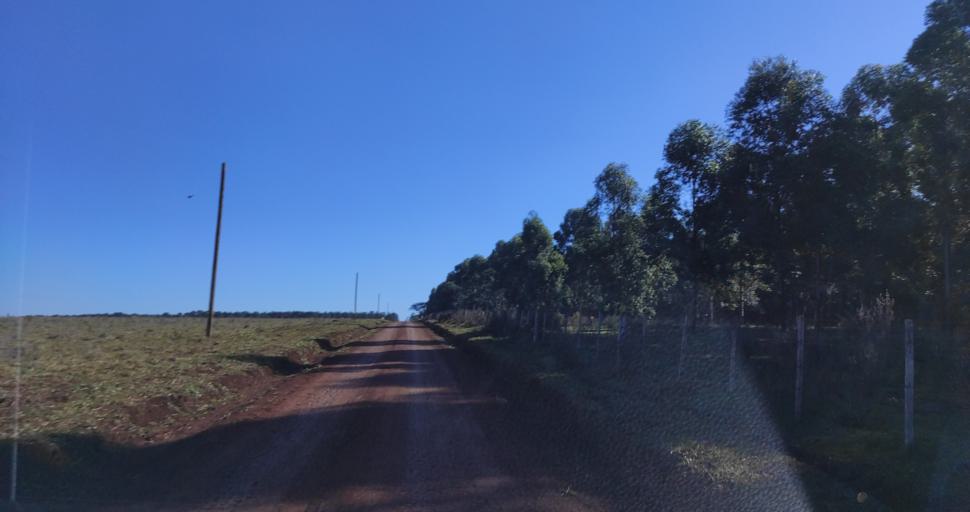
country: PY
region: Itapua
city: San Juan del Parana
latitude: -27.4234
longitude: -56.0864
